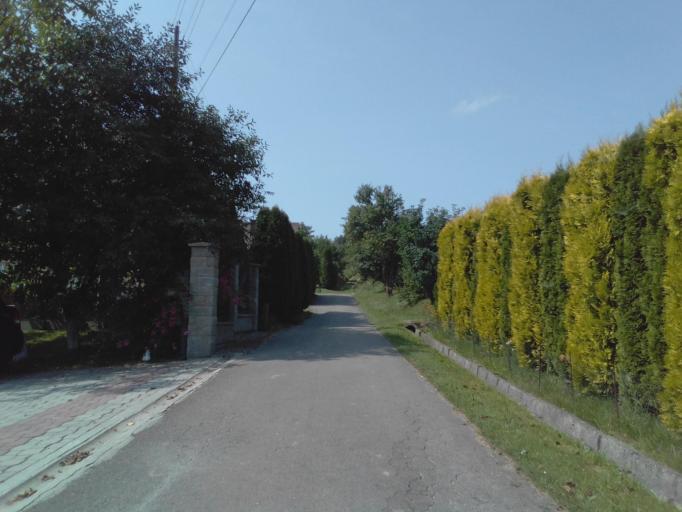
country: PL
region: Subcarpathian Voivodeship
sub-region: Powiat brzozowski
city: Domaradz
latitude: 49.7904
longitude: 21.9385
